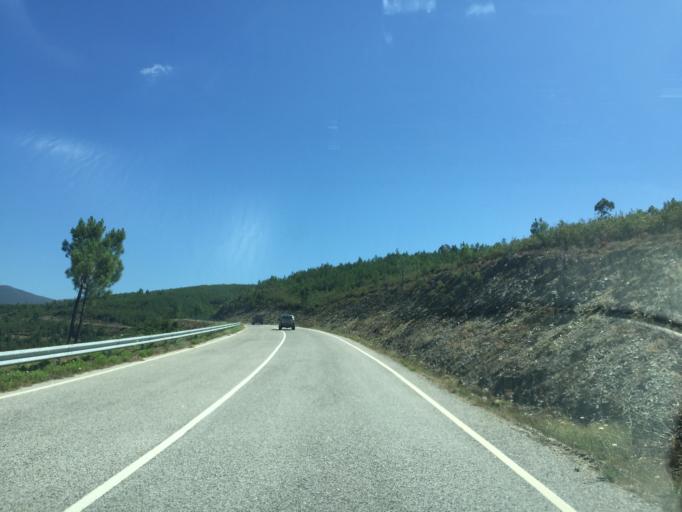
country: PT
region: Coimbra
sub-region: Pampilhosa da Serra
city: Pampilhosa da Serra
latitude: 40.1095
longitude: -7.8282
